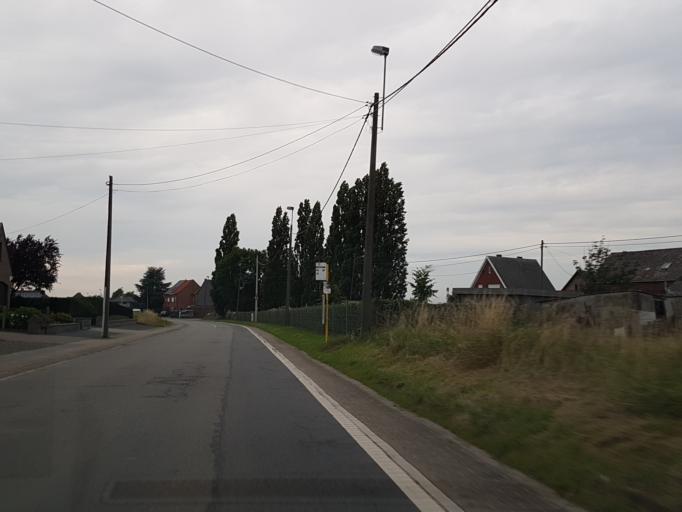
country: BE
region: Flanders
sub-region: Provincie Vlaams-Brabant
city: Kapelle-op-den-Bos
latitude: 50.9966
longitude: 4.3656
